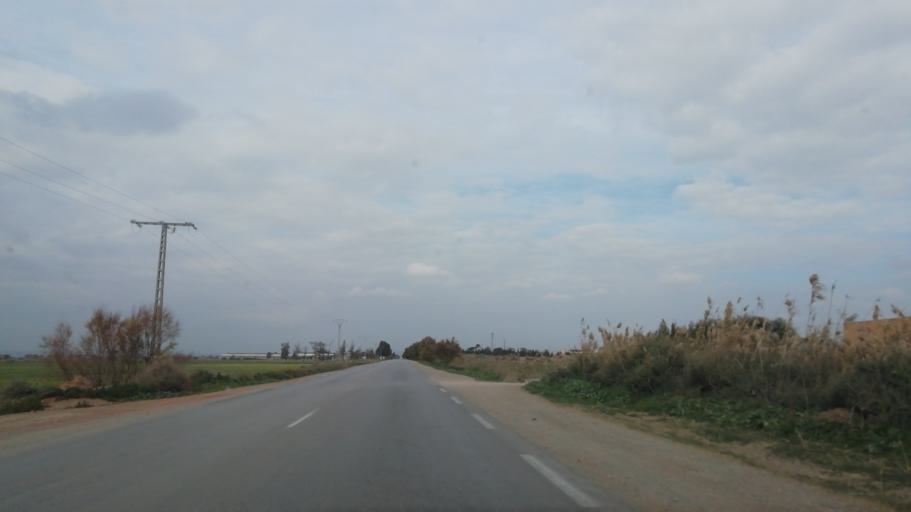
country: DZ
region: Mascara
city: Mascara
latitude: 35.6474
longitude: 0.0598
